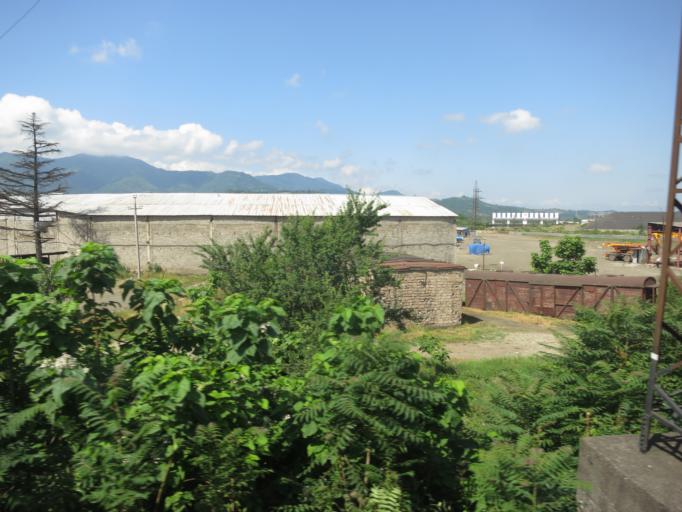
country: GE
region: Imereti
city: Zestap'oni
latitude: 42.1122
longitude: 43.0225
